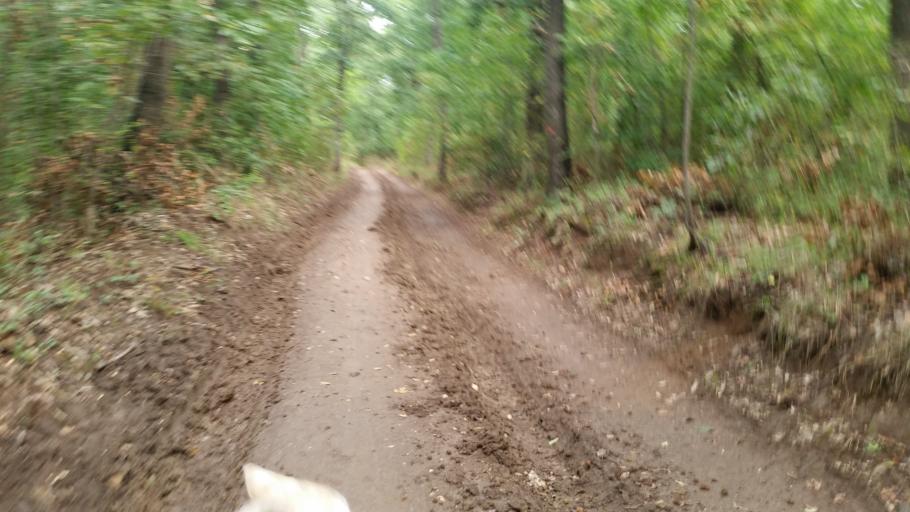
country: HU
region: Pest
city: Telki
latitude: 47.5630
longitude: 18.8247
